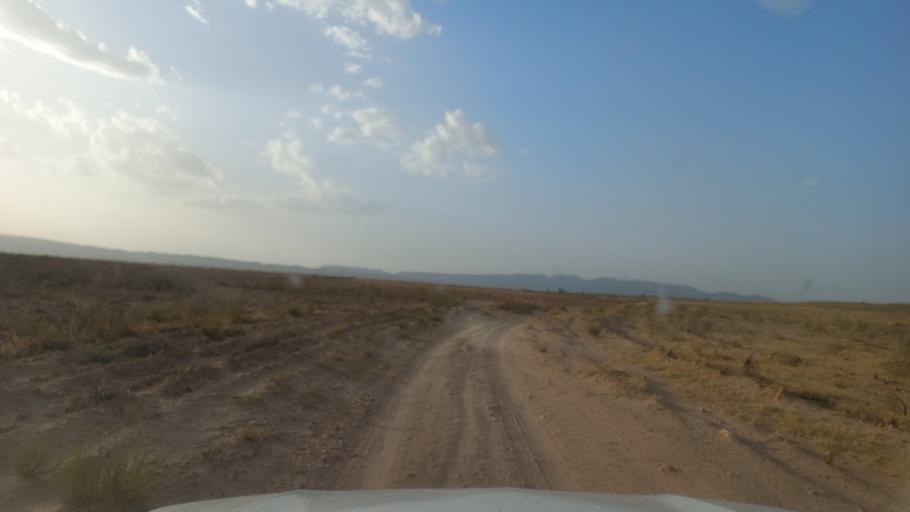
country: TN
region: Al Qasrayn
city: Sbiba
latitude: 35.3049
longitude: 9.0747
